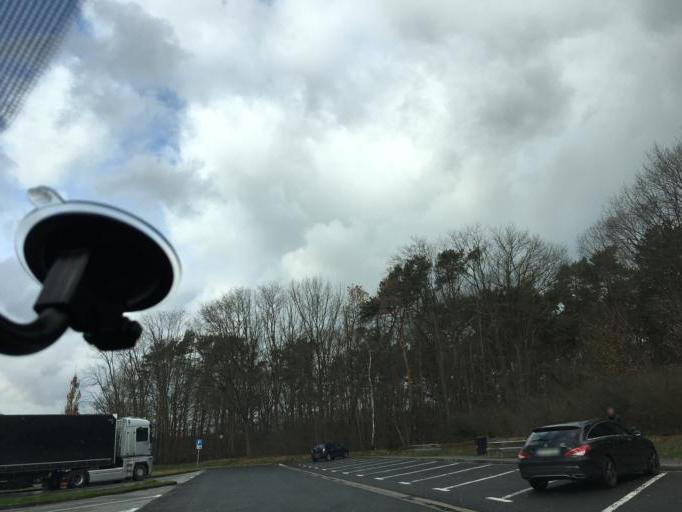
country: DE
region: North Rhine-Westphalia
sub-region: Regierungsbezirk Dusseldorf
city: Wesel
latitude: 51.7051
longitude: 6.6411
